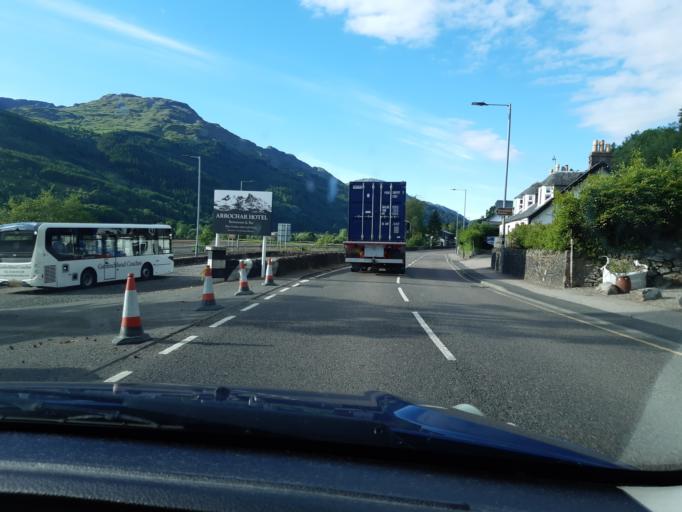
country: GB
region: Scotland
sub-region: Argyll and Bute
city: Garelochhead
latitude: 56.2003
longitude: -4.7456
